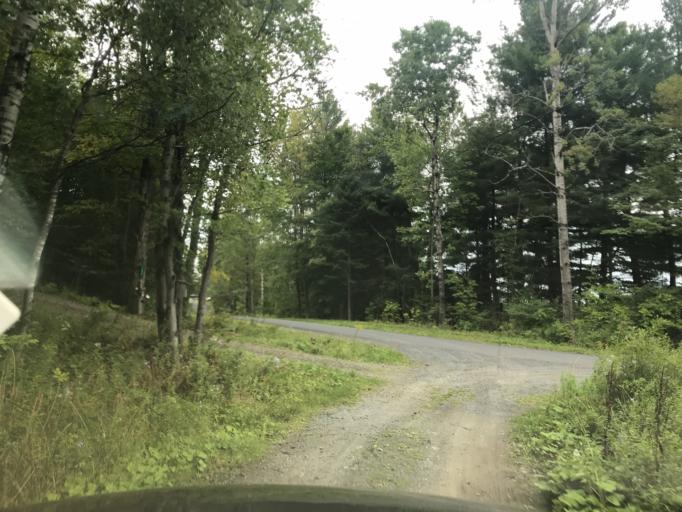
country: US
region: New York
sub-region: Otsego County
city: Worcester
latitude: 42.5310
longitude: -74.6617
